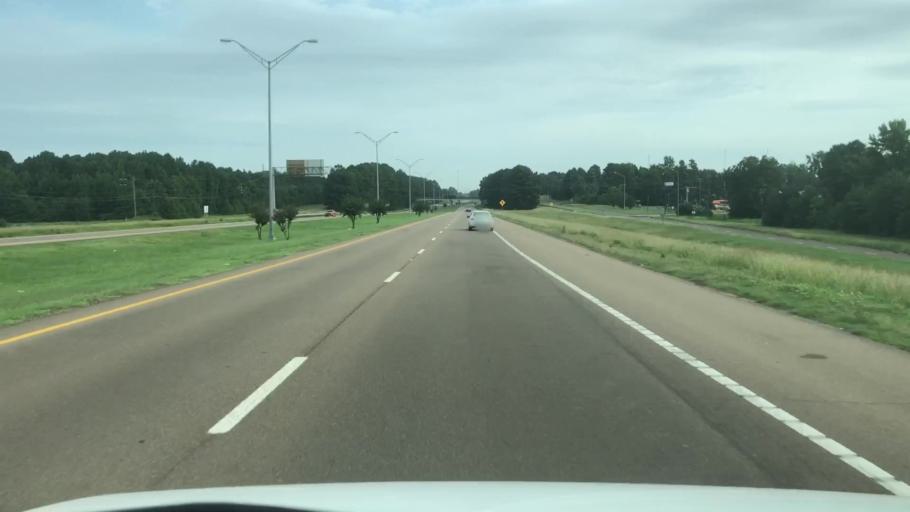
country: US
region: Texas
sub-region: Bowie County
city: Wake Village
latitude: 33.4054
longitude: -94.0974
